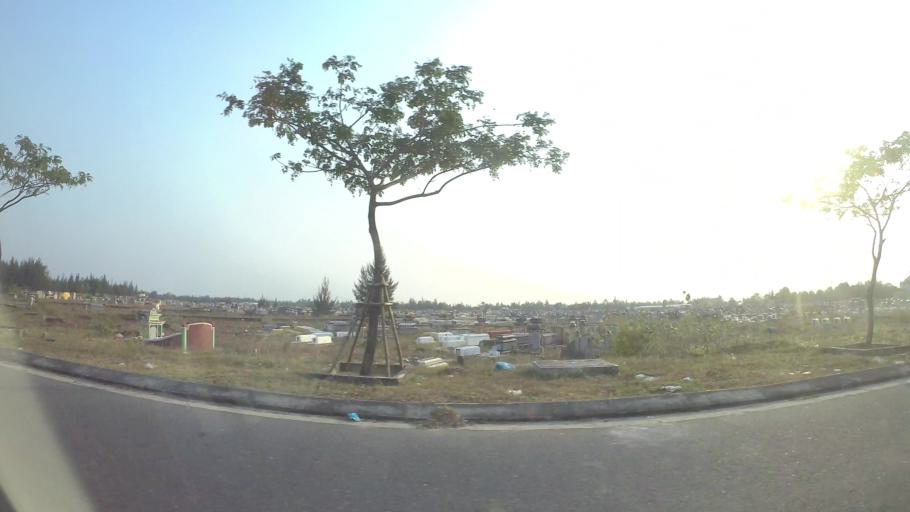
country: VN
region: Da Nang
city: Ngu Hanh Son
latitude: 15.9839
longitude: 108.2428
